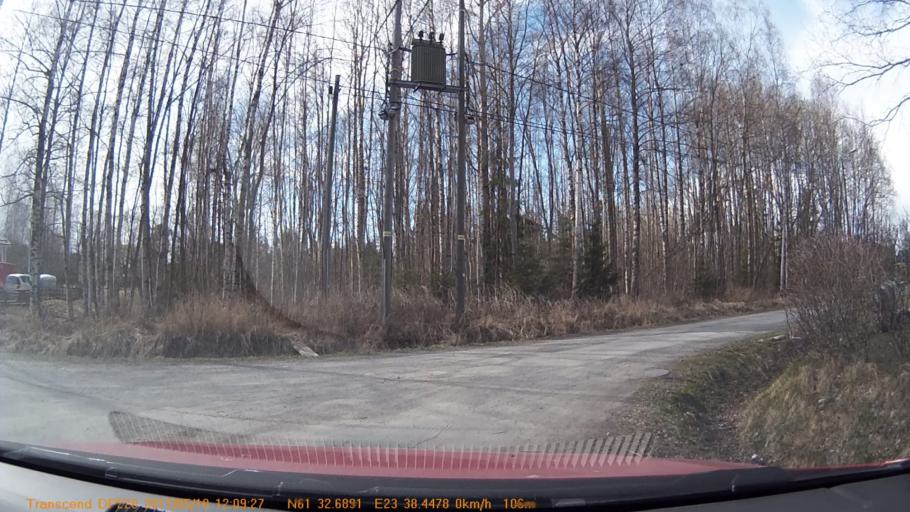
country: FI
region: Pirkanmaa
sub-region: Tampere
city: Yloejaervi
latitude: 61.5448
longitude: 23.6408
